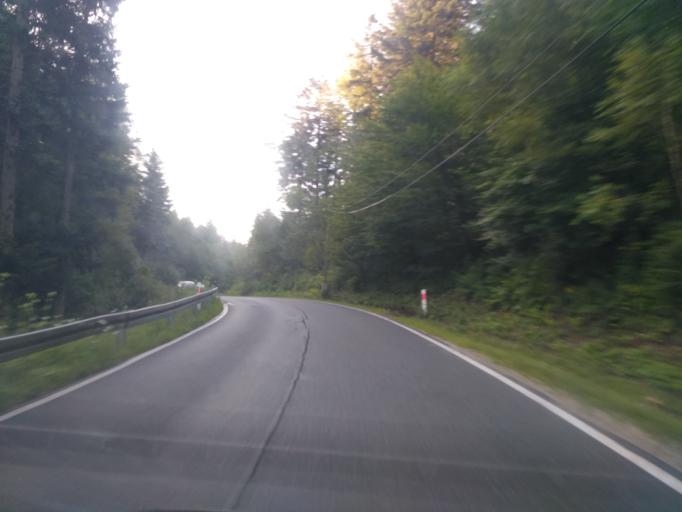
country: PL
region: Subcarpathian Voivodeship
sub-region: Powiat krosnienski
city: Korczyna
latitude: 49.7503
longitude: 21.8009
